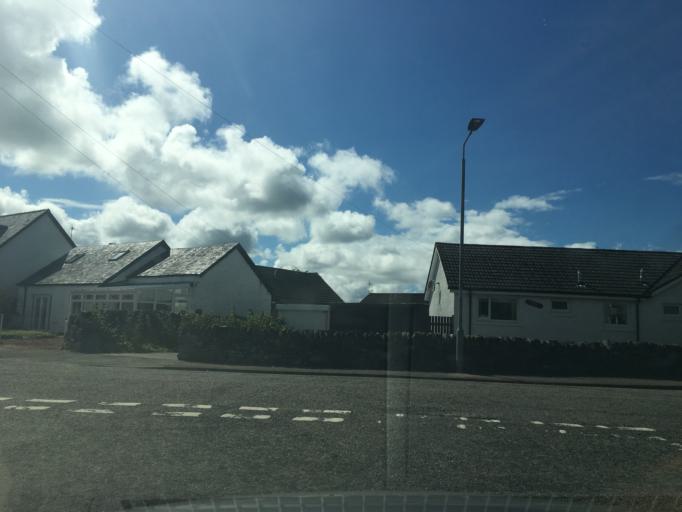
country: GB
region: Scotland
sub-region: Argyll and Bute
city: Lochgilphead
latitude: 56.0807
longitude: -5.4510
